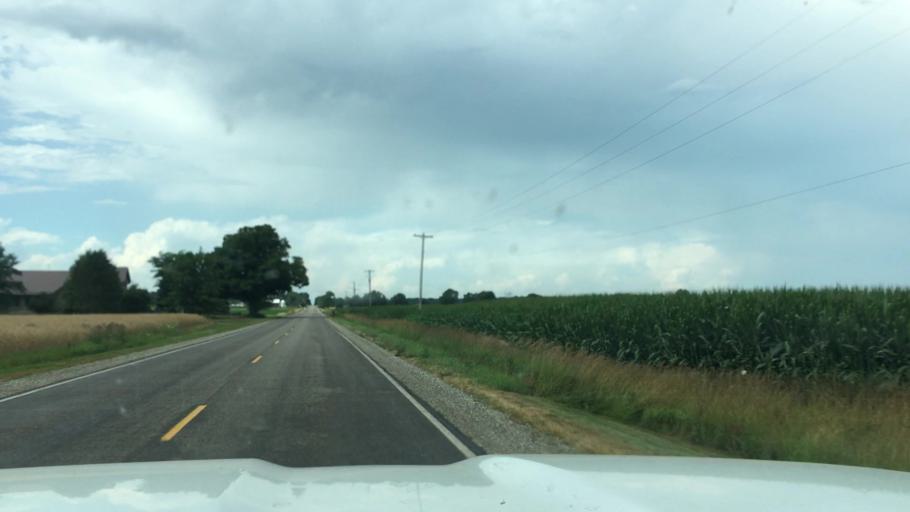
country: US
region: Michigan
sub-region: Montcalm County
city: Carson City
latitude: 43.2233
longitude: -84.7776
